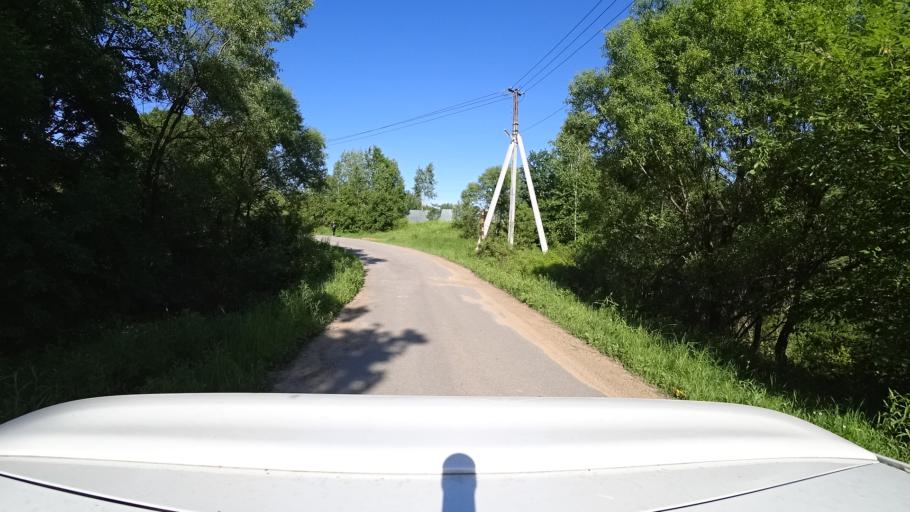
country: RU
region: Khabarovsk Krai
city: Topolevo
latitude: 48.5459
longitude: 135.1839
